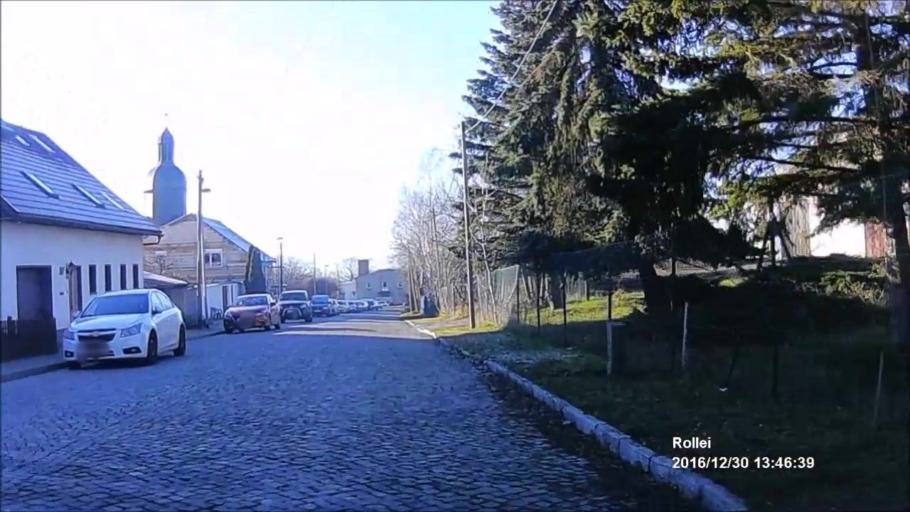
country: DE
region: Thuringia
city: Rockhausen
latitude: 50.9192
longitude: 11.0567
